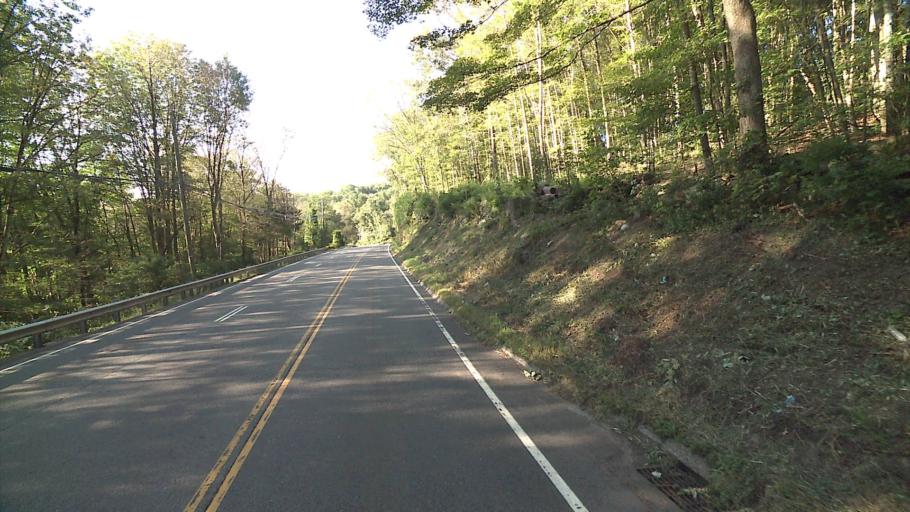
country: US
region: Connecticut
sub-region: New London County
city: Baltic
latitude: 41.6131
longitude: -72.1451
